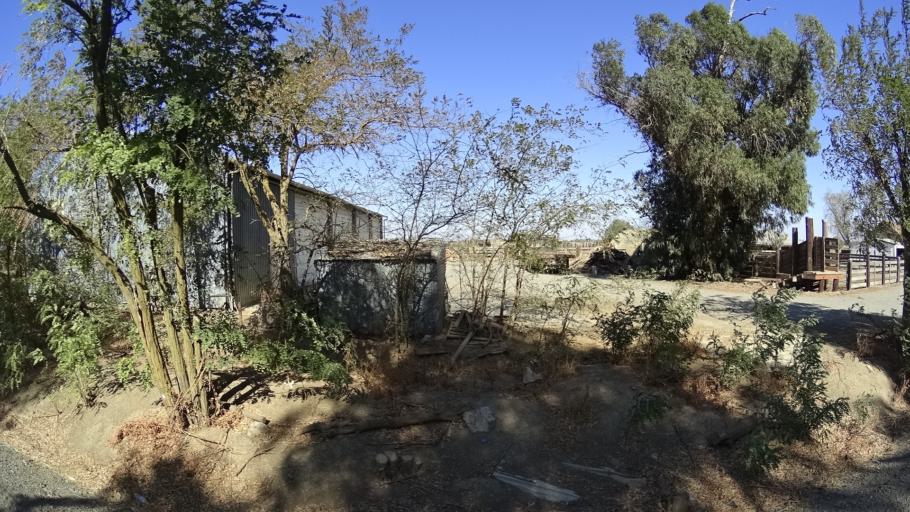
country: US
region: California
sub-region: Yolo County
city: Cottonwood
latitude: 38.6198
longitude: -121.8876
